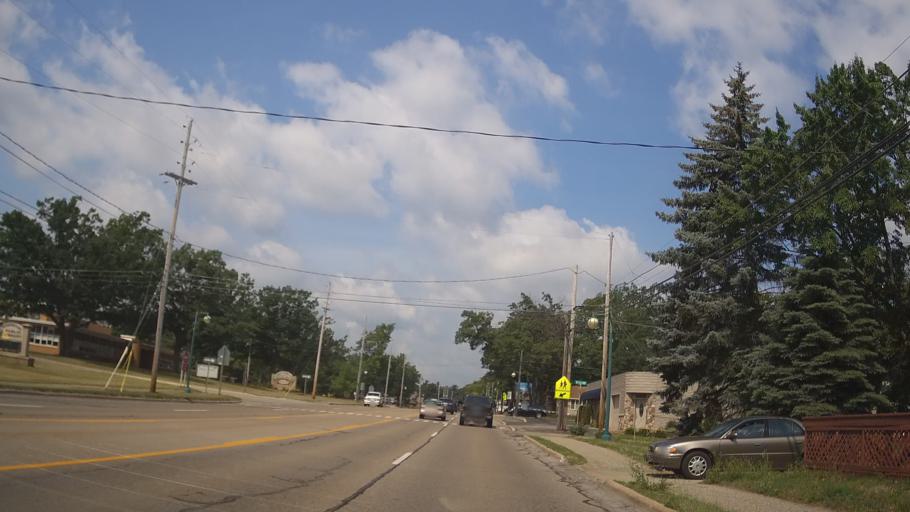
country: US
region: Michigan
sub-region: Roscommon County
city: Houghton Lake
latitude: 44.2984
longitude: -84.7263
